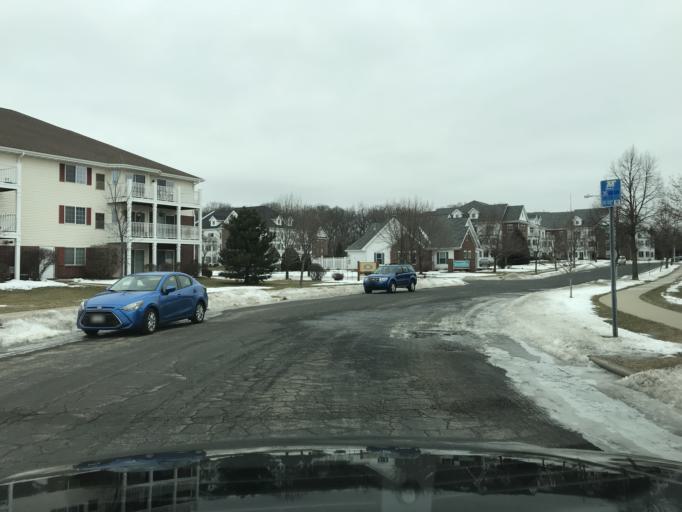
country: US
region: Wisconsin
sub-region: Dane County
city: Monona
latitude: 43.0755
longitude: -89.2780
